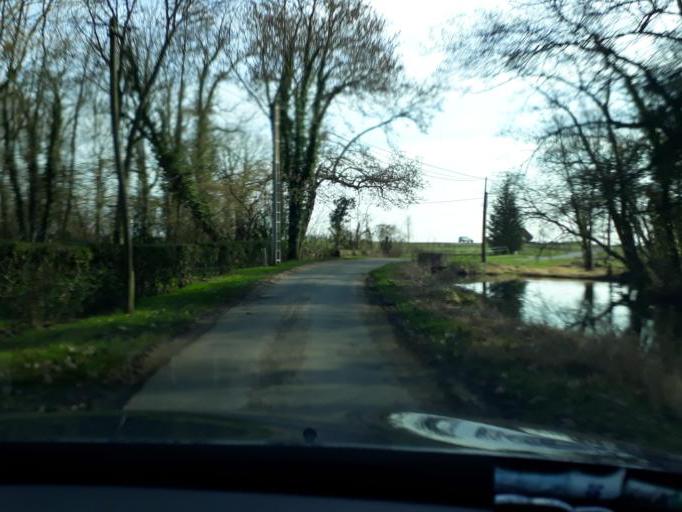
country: FR
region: Centre
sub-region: Departement du Loiret
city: Meung-sur-Loire
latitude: 47.8643
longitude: 1.6715
